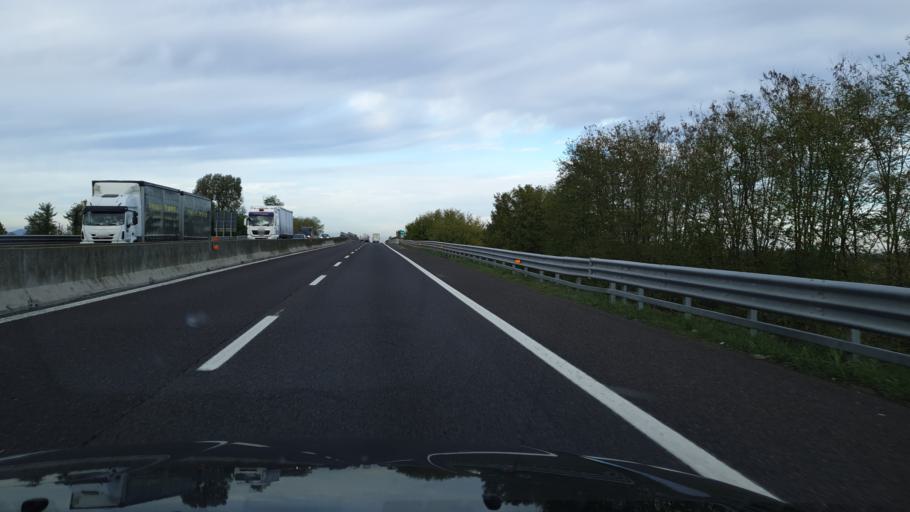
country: IT
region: Veneto
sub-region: Provincia di Rovigo
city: Costa di Rovigo
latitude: 45.0496
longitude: 11.7165
